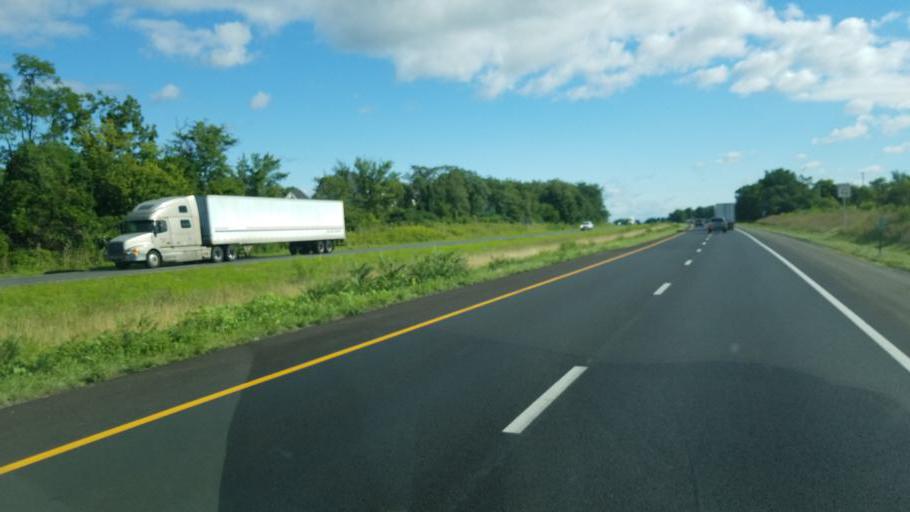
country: US
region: Virginia
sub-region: Frederick County
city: Stephens City
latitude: 39.0879
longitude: -78.2098
